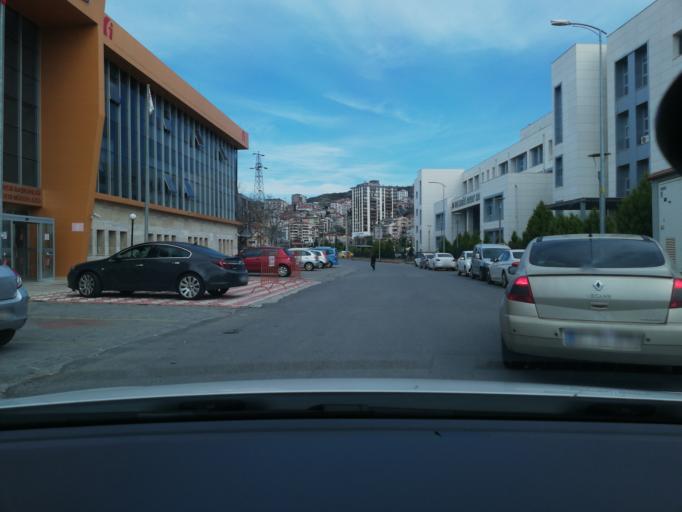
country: TR
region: Zonguldak
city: Eregli
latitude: 41.2912
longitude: 31.4068
